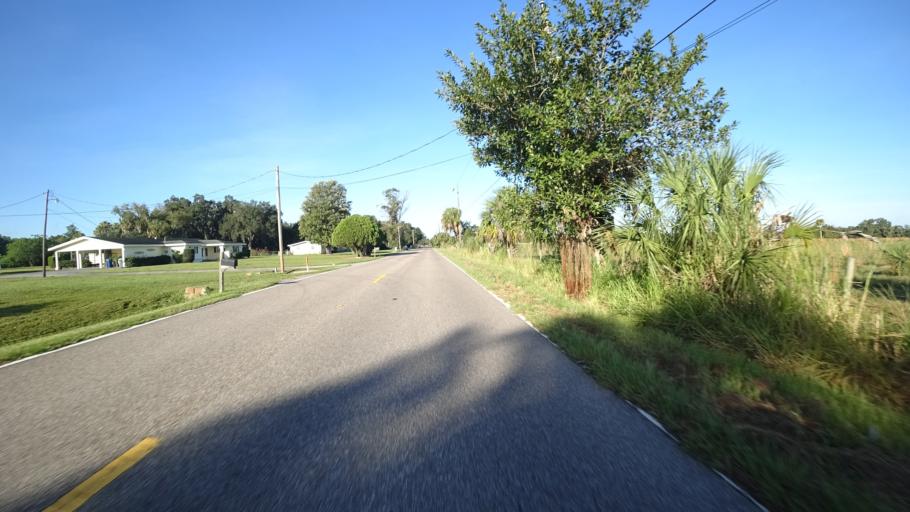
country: US
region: Florida
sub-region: Manatee County
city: Memphis
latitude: 27.5682
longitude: -82.5371
